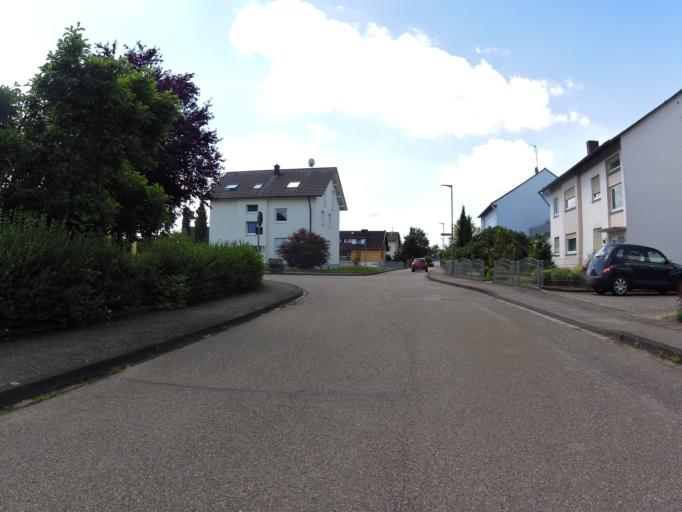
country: DE
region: Baden-Wuerttemberg
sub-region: Freiburg Region
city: Kippenheim
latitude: 48.3326
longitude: 7.8194
